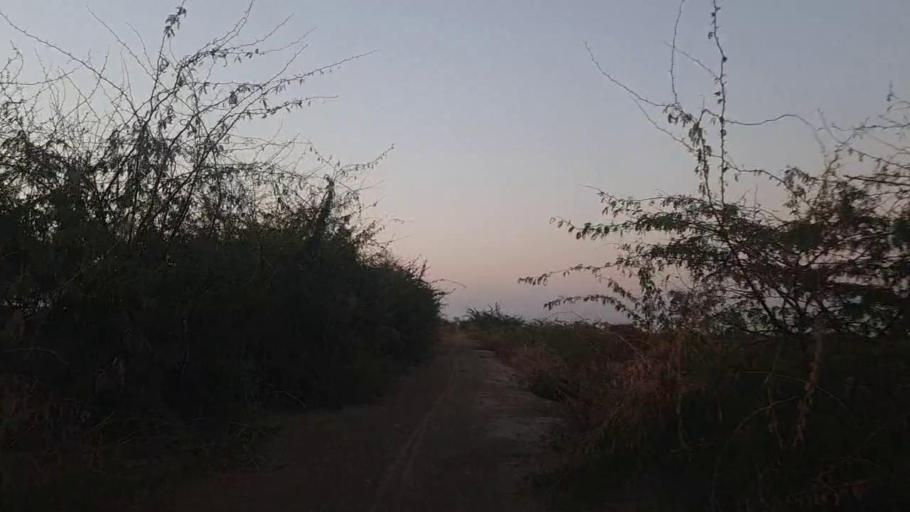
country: PK
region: Sindh
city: Tando Mittha Khan
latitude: 26.0818
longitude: 69.1515
